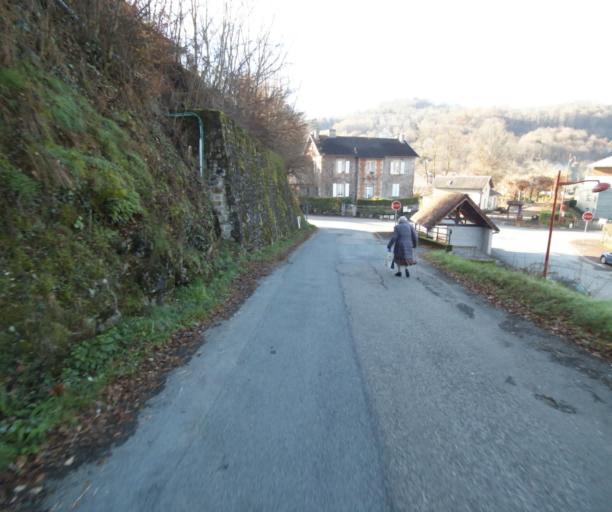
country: FR
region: Limousin
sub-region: Departement de la Correze
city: Laguenne
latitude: 45.2452
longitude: 1.7784
